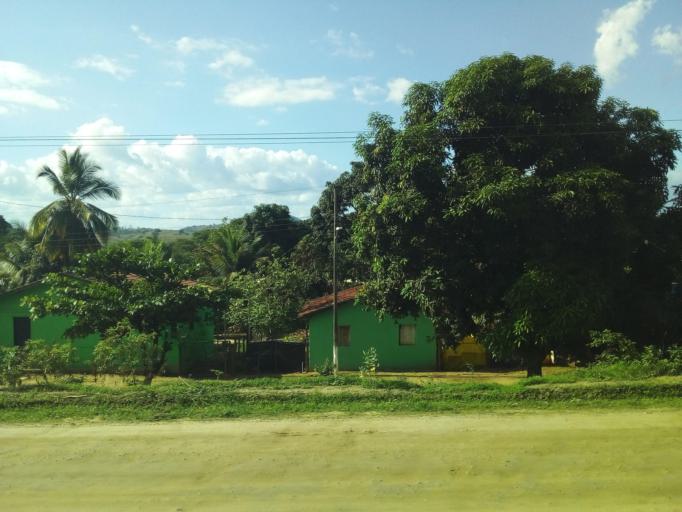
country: BR
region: Minas Gerais
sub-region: Conselheiro Pena
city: Conselheiro Pena
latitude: -19.0128
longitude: -41.5476
